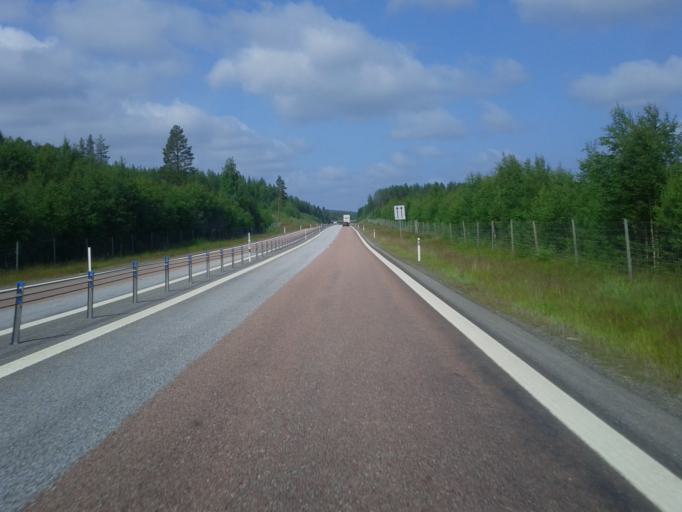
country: SE
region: Vaesterbotten
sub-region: Skelleftea Kommun
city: Soedra Bergsbyn
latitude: 64.6926
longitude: 21.0311
